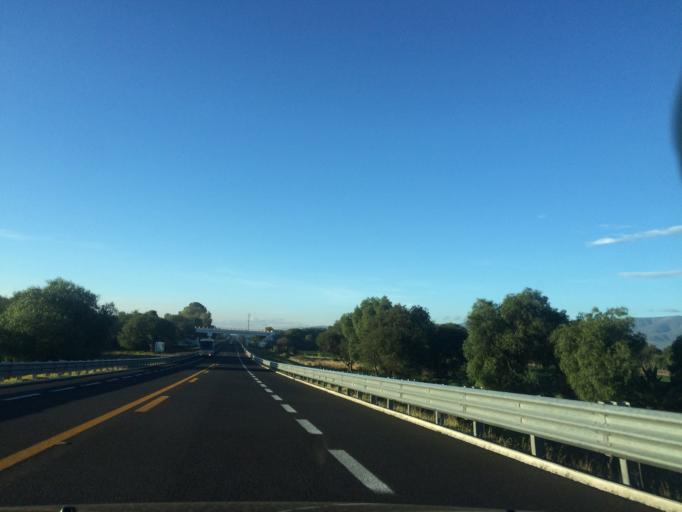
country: MX
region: Puebla
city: Santiago Miahuatlan
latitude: 18.5435
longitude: -97.4610
